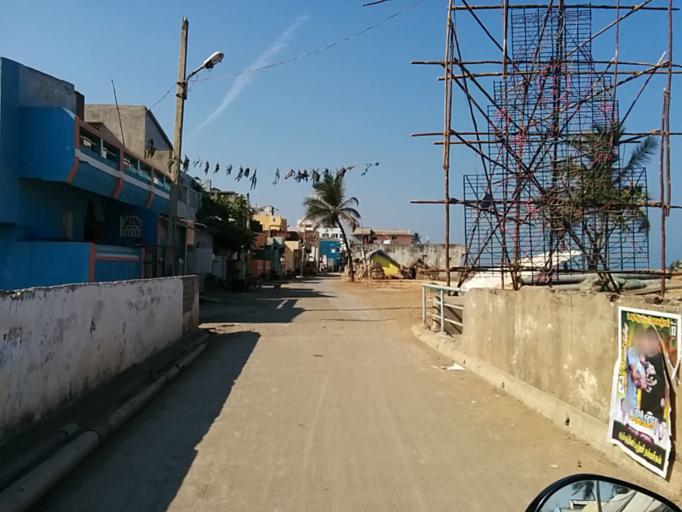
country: IN
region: Pondicherry
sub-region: Puducherry
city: Puducherry
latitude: 11.9436
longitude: 79.8372
